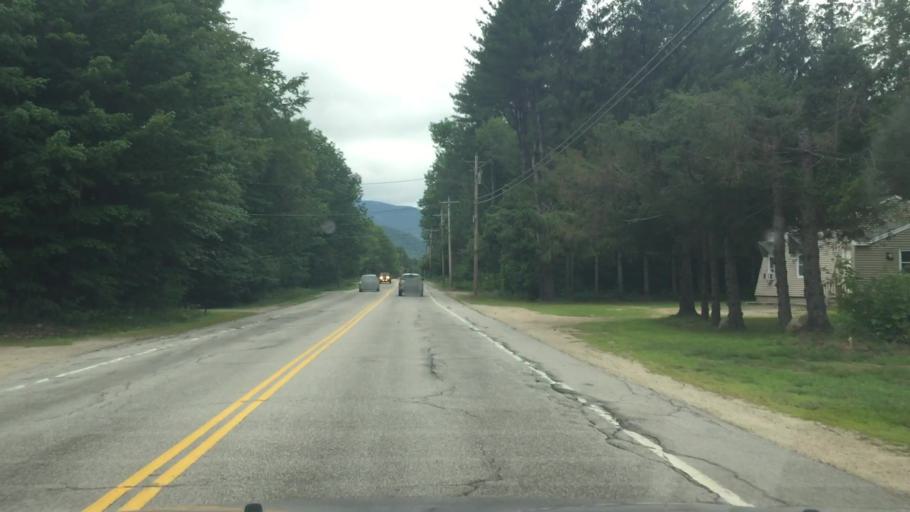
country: US
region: New Hampshire
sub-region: Carroll County
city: North Conway
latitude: 44.0791
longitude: -71.2626
